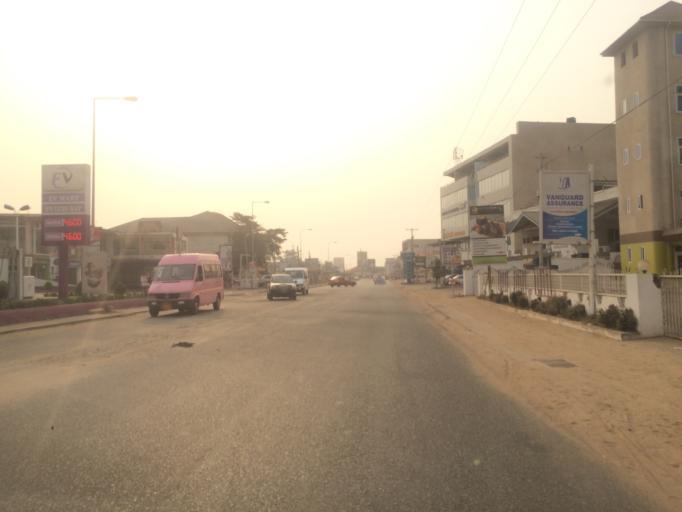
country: GH
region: Greater Accra
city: Nungua
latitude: 5.6231
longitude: -0.0729
